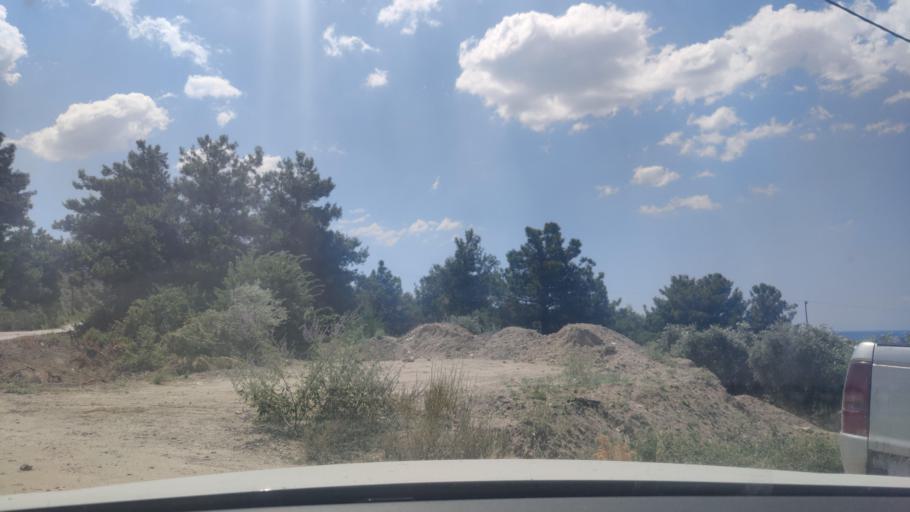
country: GR
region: East Macedonia and Thrace
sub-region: Nomos Kavalas
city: Limenaria
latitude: 40.6390
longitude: 24.5261
